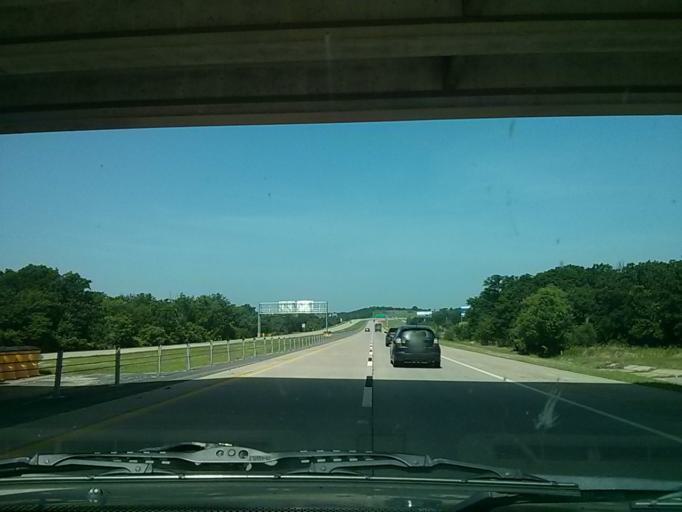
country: US
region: Oklahoma
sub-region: Tulsa County
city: Glenpool
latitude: 36.0092
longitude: -96.0268
